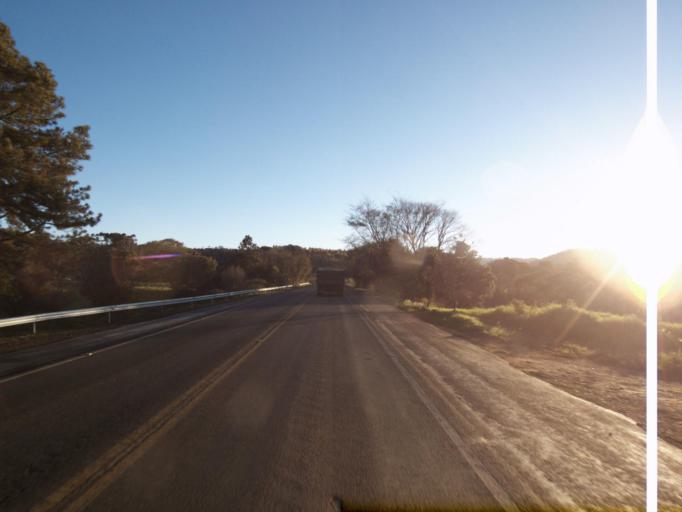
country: BR
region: Santa Catarina
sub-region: Sao Lourenco Do Oeste
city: Sao Lourenco dOeste
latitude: -26.8295
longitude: -53.1215
